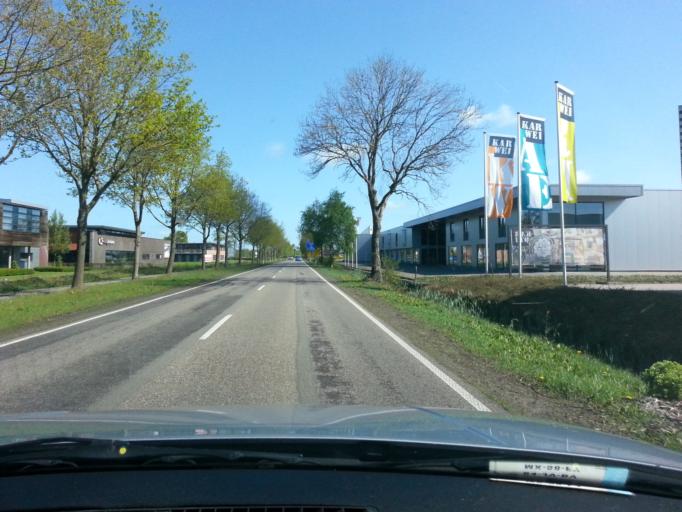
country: NL
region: Friesland
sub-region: Gemeente Achtkarspelen
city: Surhuisterveen
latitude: 53.1736
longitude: 6.1828
